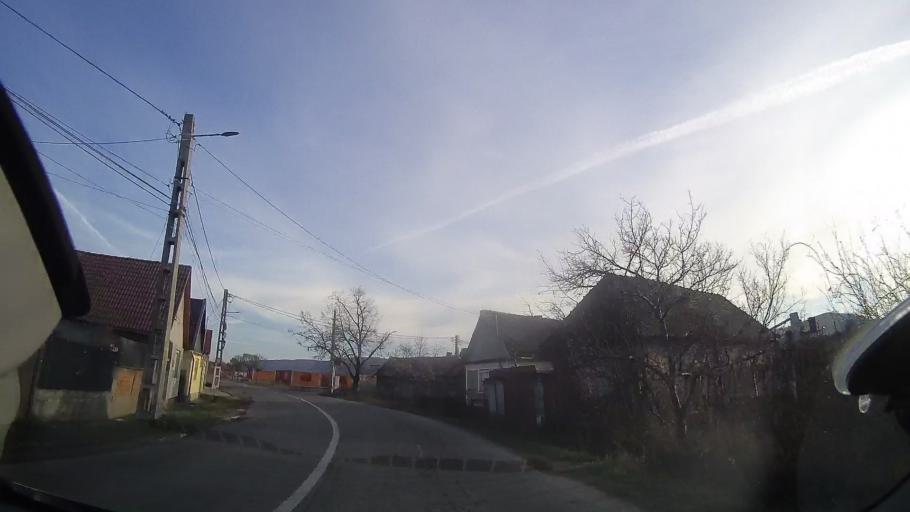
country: RO
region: Bihor
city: Lugasu de Jos
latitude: 47.0450
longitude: 22.3319
